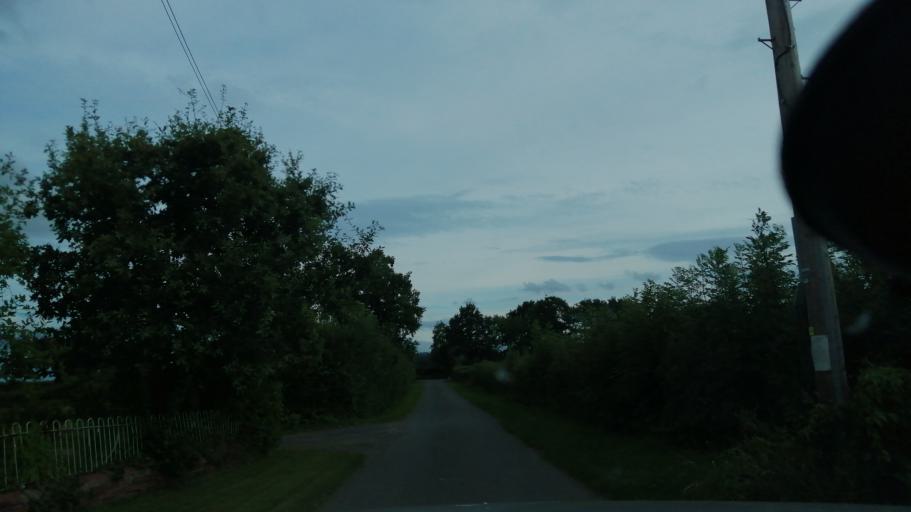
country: GB
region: England
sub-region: Herefordshire
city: Thruxton
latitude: 52.0082
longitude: -2.7971
